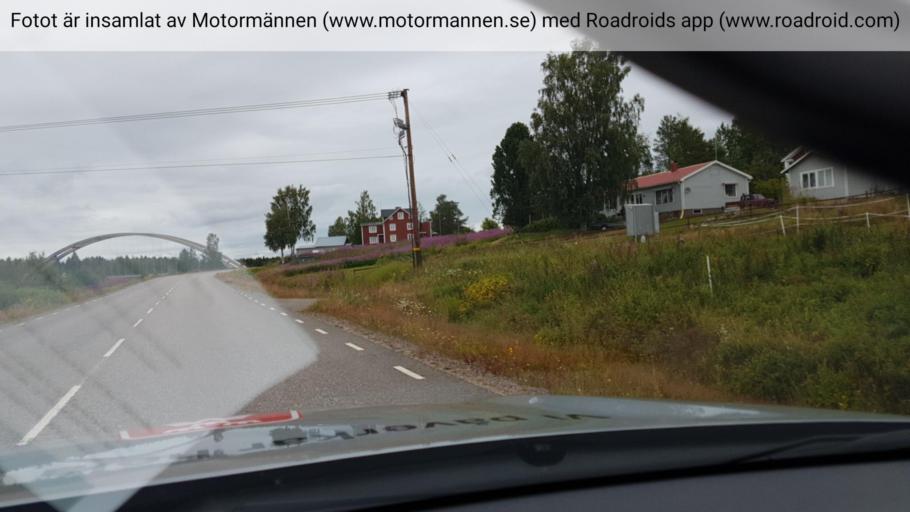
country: SE
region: Norrbotten
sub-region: Pajala Kommun
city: Pajala
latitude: 67.1656
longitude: 22.6183
